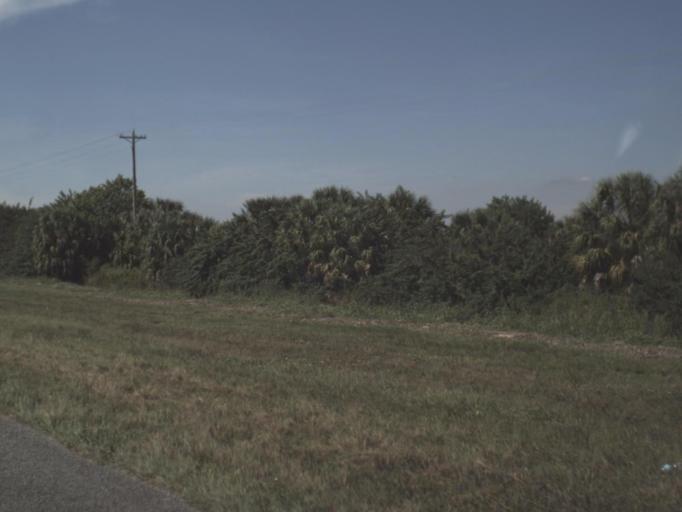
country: US
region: Florida
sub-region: Glades County
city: Moore Haven
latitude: 26.8338
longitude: -81.1799
